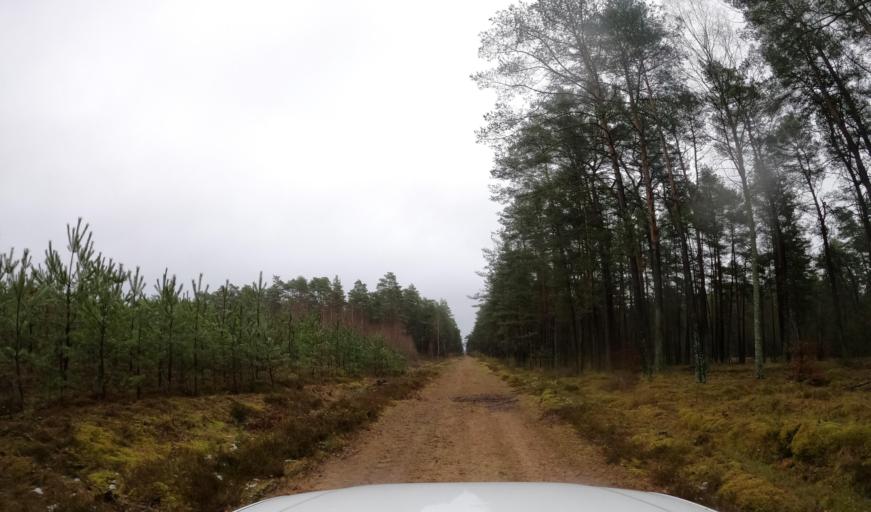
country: PL
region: West Pomeranian Voivodeship
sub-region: Powiat szczecinecki
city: Borne Sulinowo
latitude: 53.5872
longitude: 16.4804
